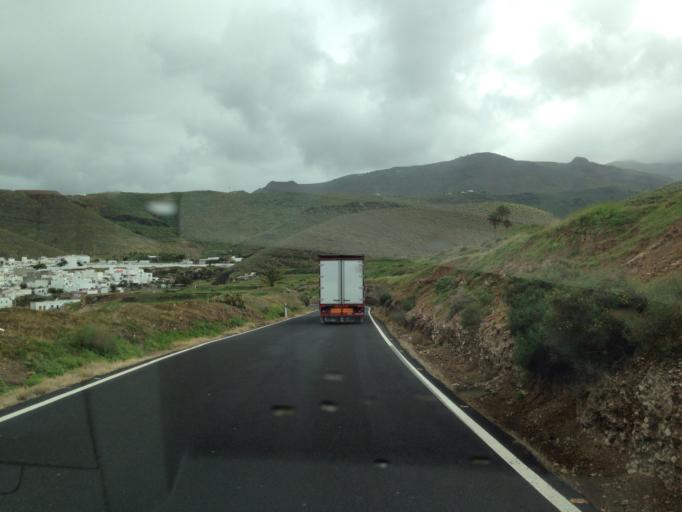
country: ES
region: Canary Islands
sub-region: Provincia de Las Palmas
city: Agaete
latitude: 28.0957
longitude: -15.7003
